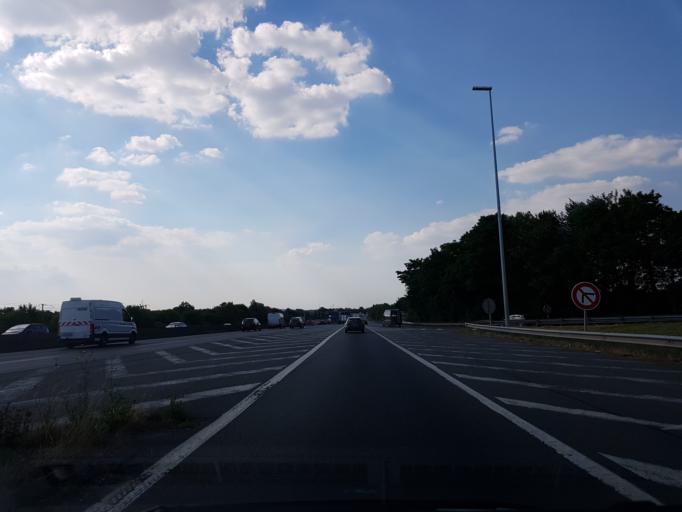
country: FR
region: Nord-Pas-de-Calais
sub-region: Departement du Pas-de-Calais
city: Dourges
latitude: 50.4316
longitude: 2.9801
